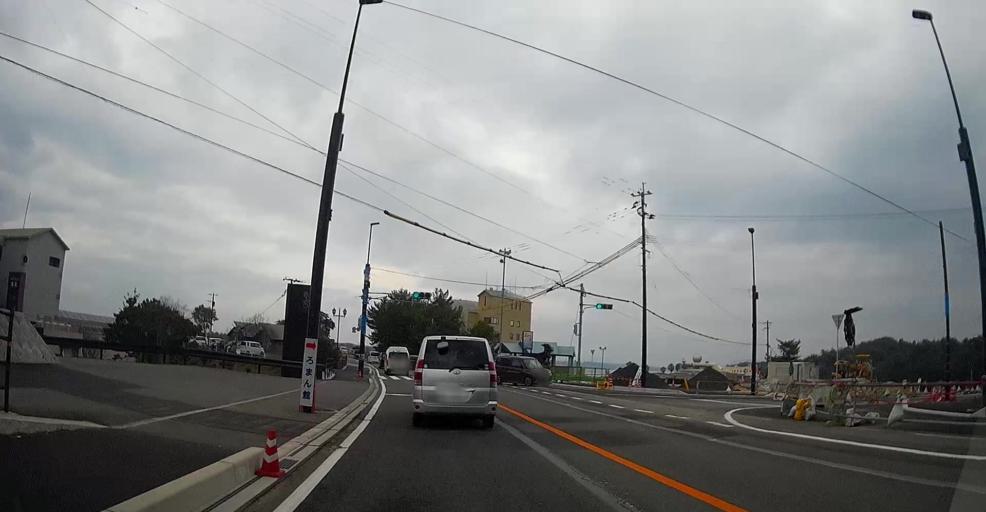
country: JP
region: Kumamoto
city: Yatsushiro
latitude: 32.5259
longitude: 130.4250
